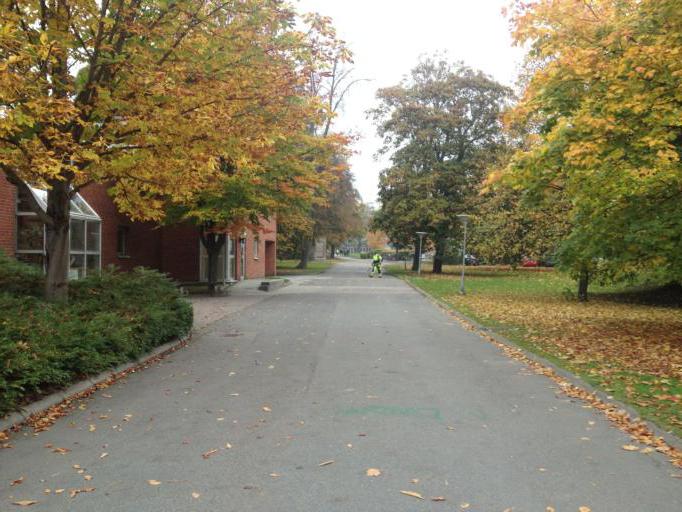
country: SE
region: Skane
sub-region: Lunds Kommun
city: Lund
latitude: 55.7129
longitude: 13.2106
